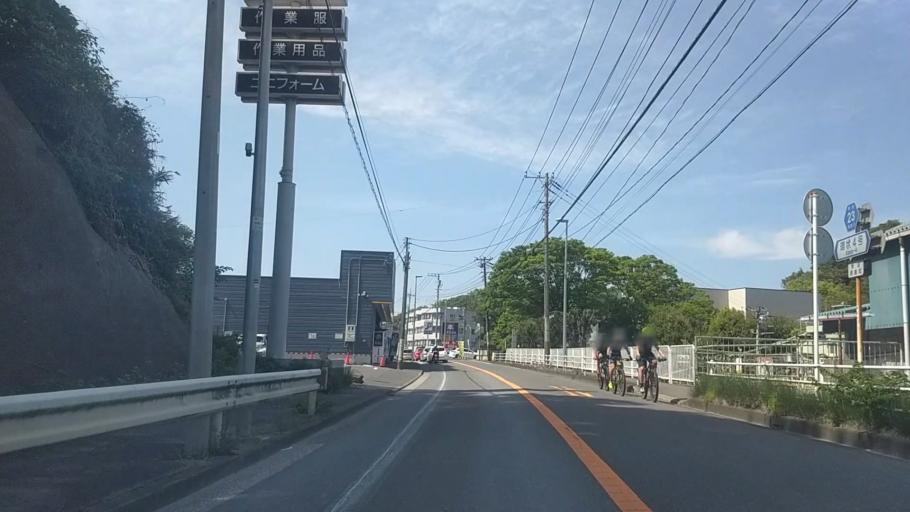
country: JP
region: Kanagawa
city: Kamakura
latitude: 35.3476
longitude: 139.5819
